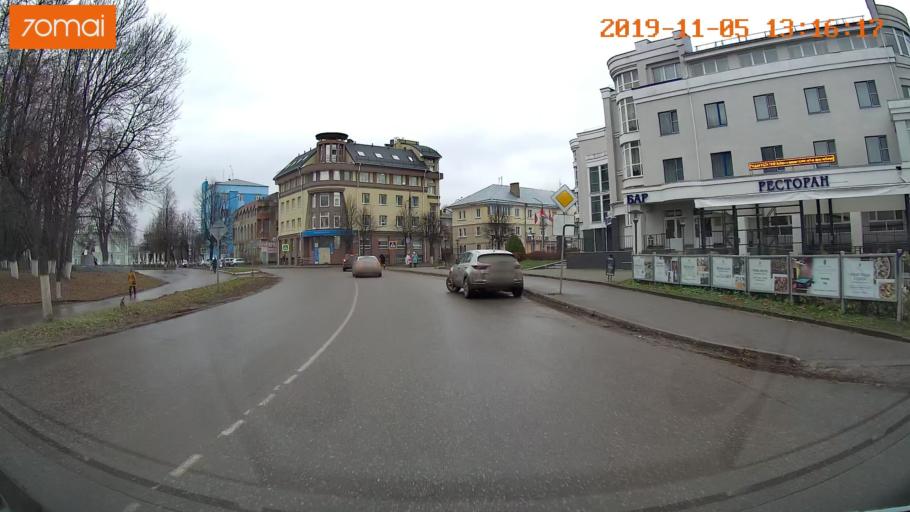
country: RU
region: Ivanovo
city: Shuya
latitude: 56.8528
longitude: 41.3750
